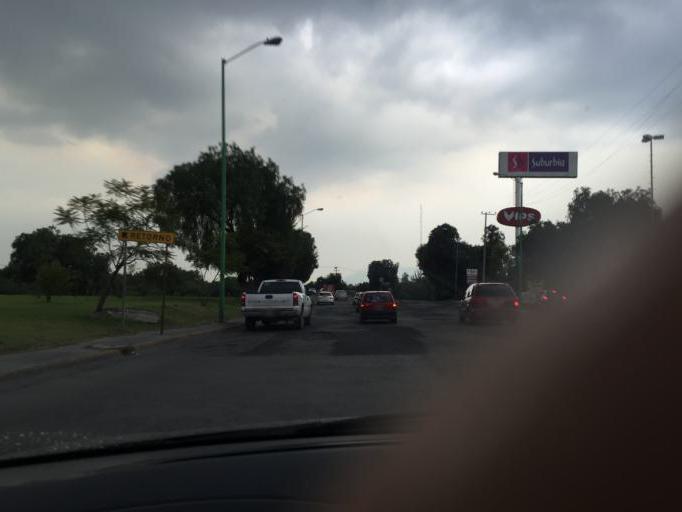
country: MX
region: Mexico
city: Cuautitlan Izcalli
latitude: 19.6549
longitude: -99.2069
